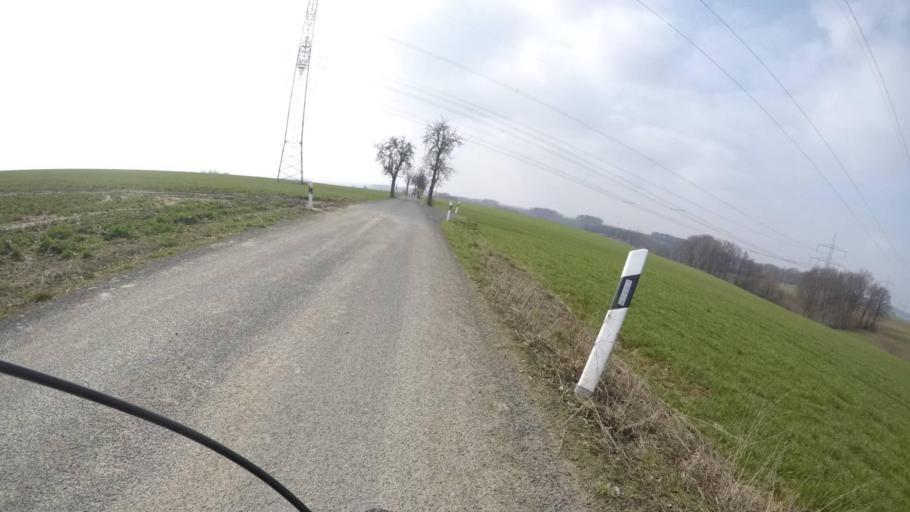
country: DE
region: Saxony
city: Niederfrohna
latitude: 50.8784
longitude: 12.6964
